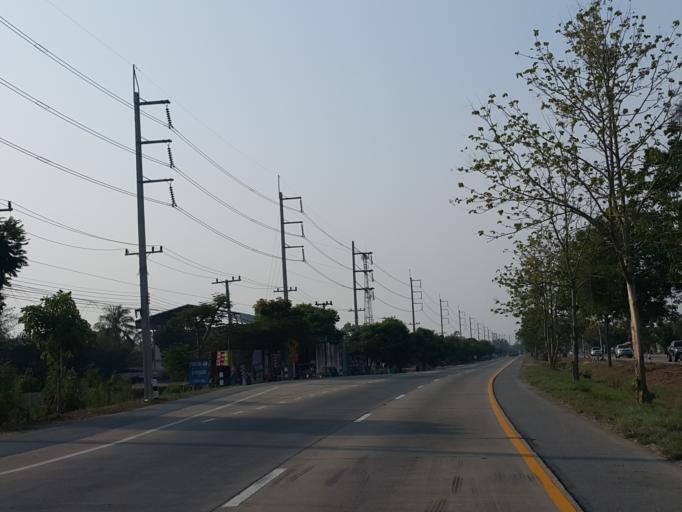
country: TH
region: Suphan Buri
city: Doem Bang Nang Buat
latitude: 14.9328
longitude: 100.0832
